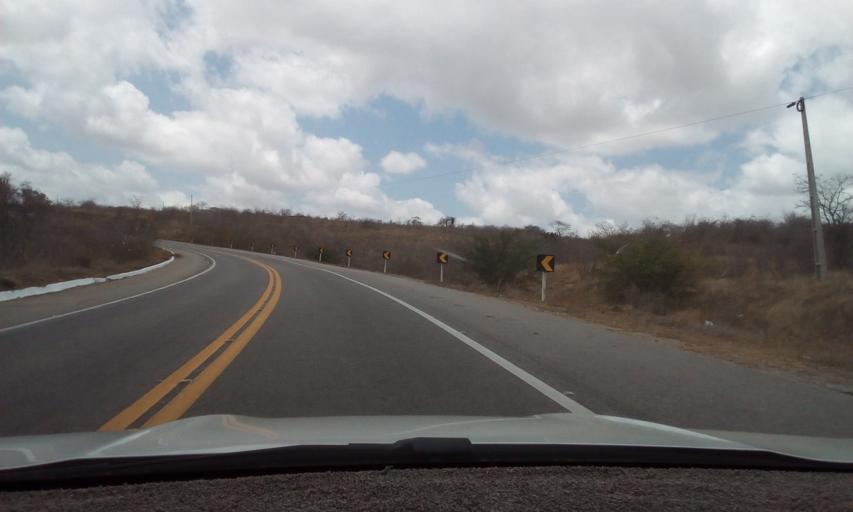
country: BR
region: Paraiba
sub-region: Boqueirao
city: Boqueirao
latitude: -7.6868
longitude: -36.0618
